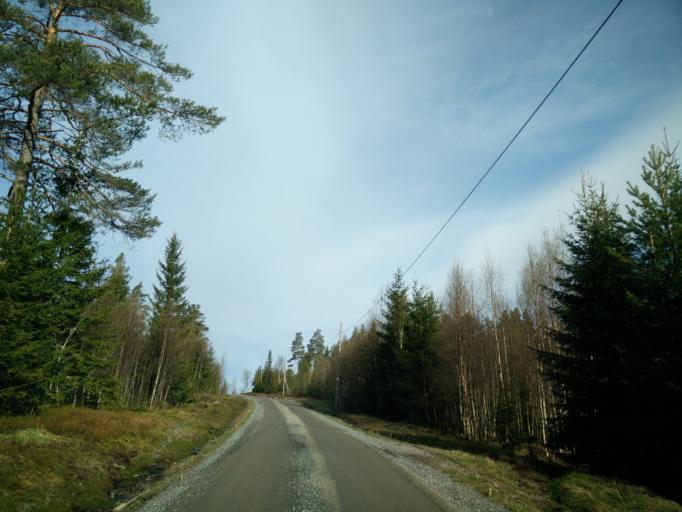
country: SE
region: Vaesternorrland
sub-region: Haernoesands Kommun
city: Haernoesand
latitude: 62.5933
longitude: 17.7578
